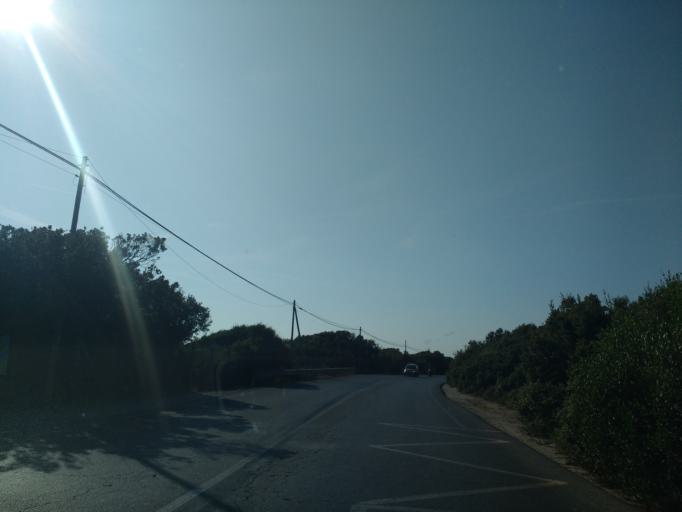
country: IT
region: Latium
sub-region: Citta metropolitana di Roma Capitale
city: Torvaianica
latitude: 41.6839
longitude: 12.3792
